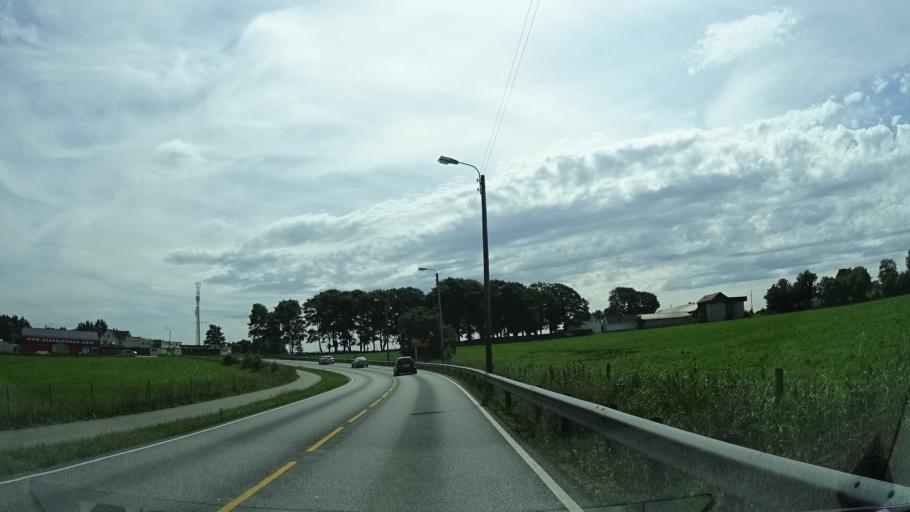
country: NO
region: Rogaland
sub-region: Randaberg
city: Randaberg
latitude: 58.9845
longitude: 5.6660
